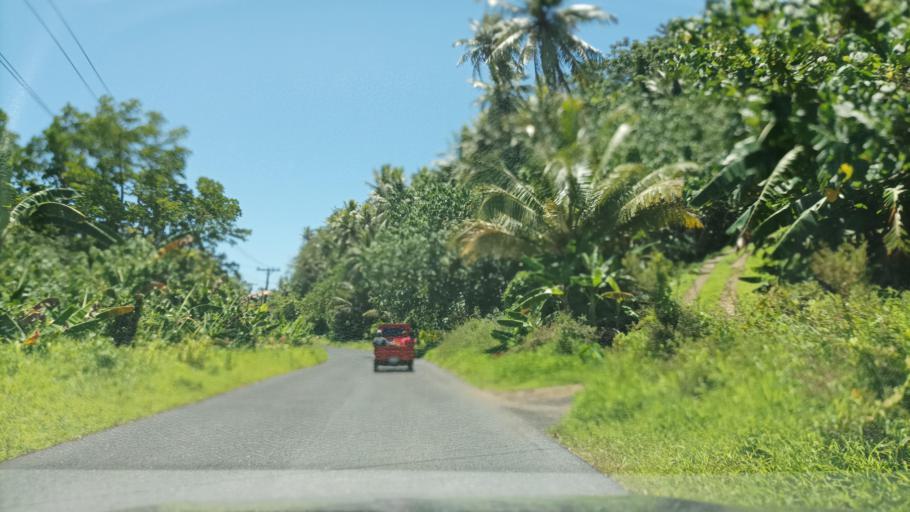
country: FM
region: Pohnpei
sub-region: Kolonia Municipality
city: Kolonia
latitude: 6.9606
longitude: 158.2745
